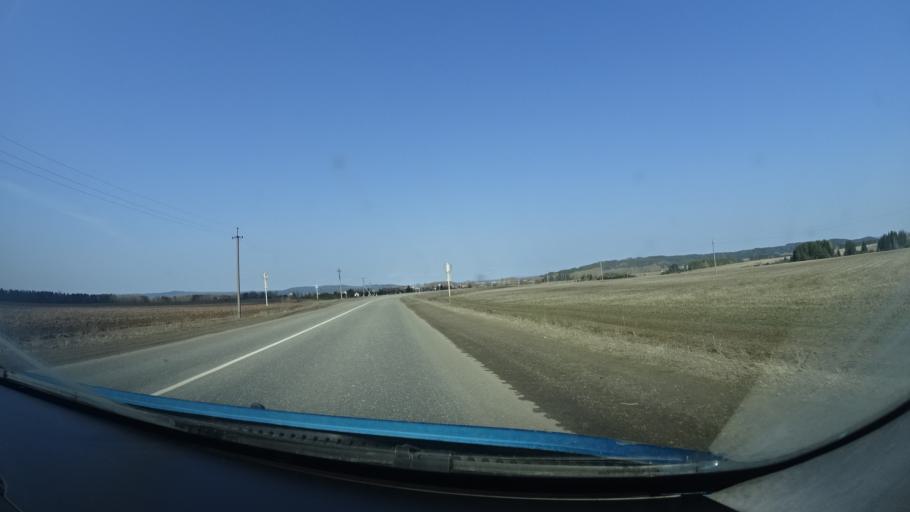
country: RU
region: Perm
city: Osa
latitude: 57.2792
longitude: 55.5665
